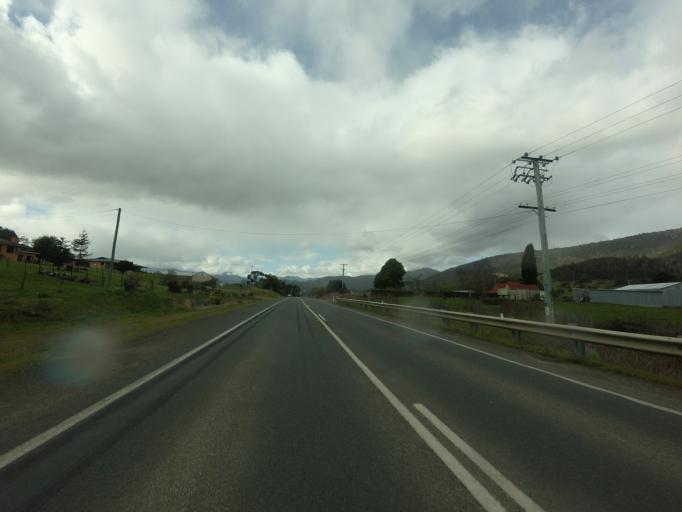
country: AU
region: Tasmania
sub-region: Huon Valley
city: Huonville
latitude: -43.0461
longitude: 147.0415
